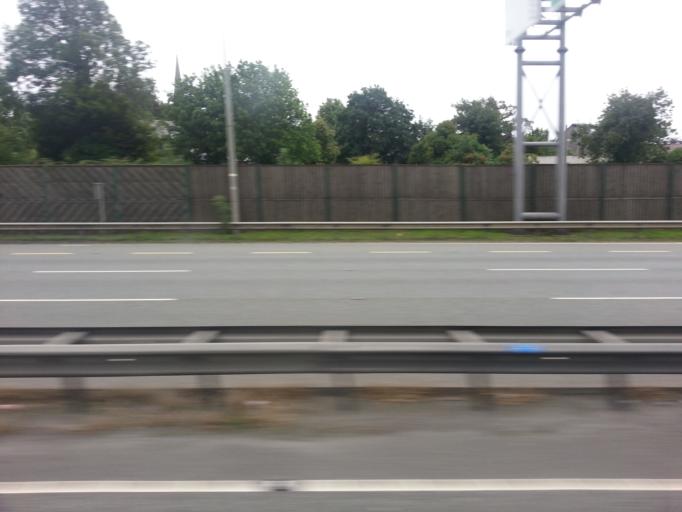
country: IE
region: Leinster
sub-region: Kildare
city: Kill
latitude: 53.2493
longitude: -6.5932
